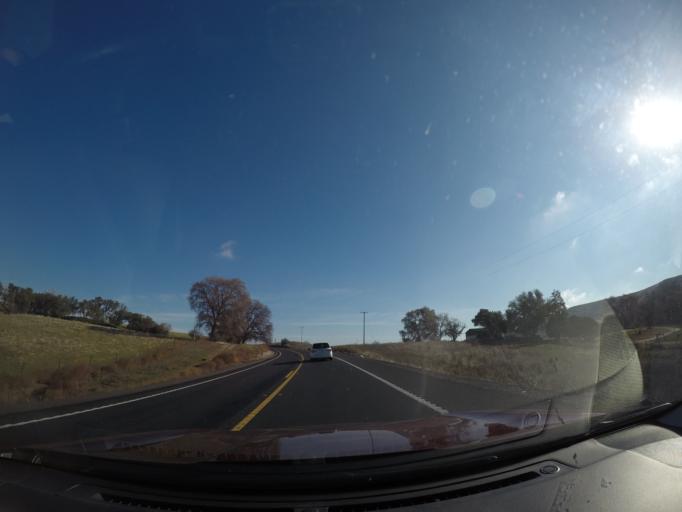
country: US
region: California
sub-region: Stanislaus County
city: East Oakdale
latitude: 37.8041
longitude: -120.6776
